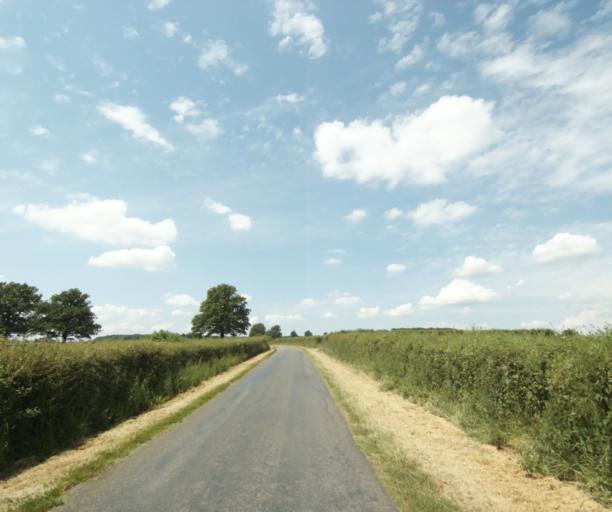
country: FR
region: Bourgogne
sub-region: Departement de Saone-et-Loire
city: Perrecy-les-Forges
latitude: 46.5821
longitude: 4.1468
